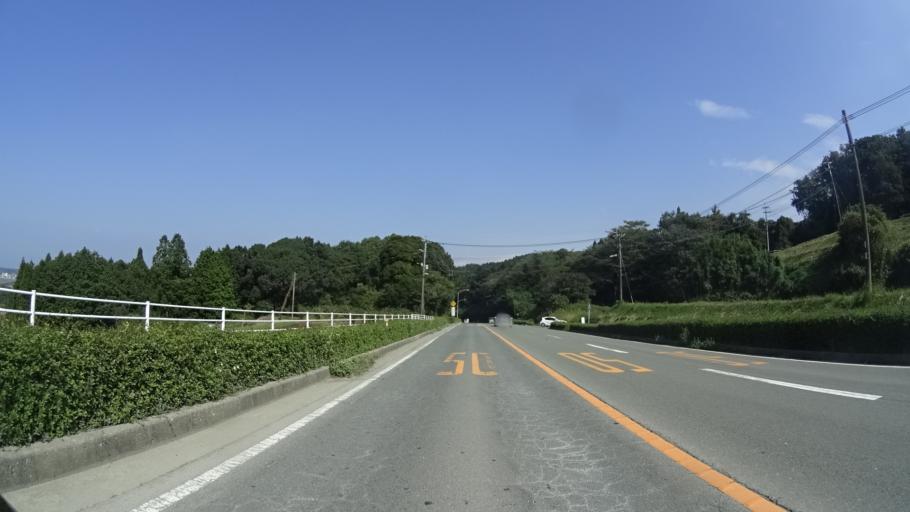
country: JP
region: Kumamoto
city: Ozu
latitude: 32.8463
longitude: 130.8589
